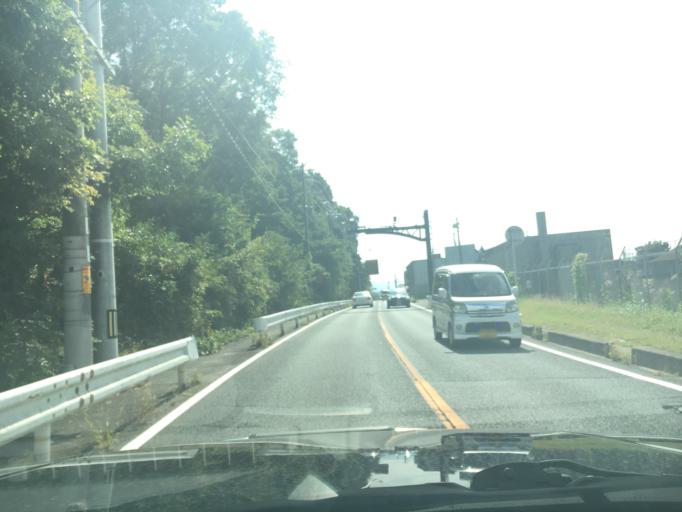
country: JP
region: Nara
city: Nara-shi
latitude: 34.7036
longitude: 135.8359
